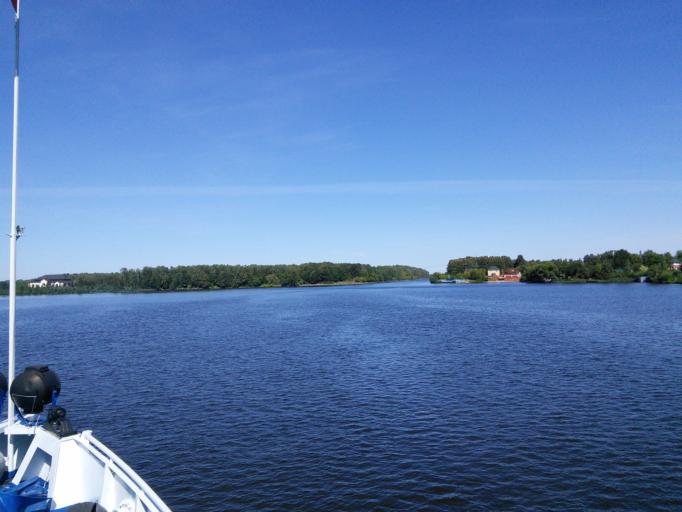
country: RU
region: Moskovskaya
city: Pirogovskiy
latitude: 56.0408
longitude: 37.6679
